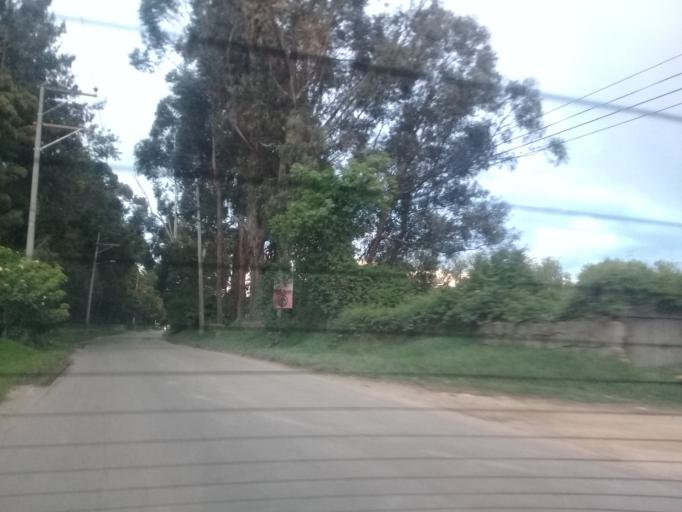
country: CO
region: Cundinamarca
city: Cajica
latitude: 4.9273
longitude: -74.0585
